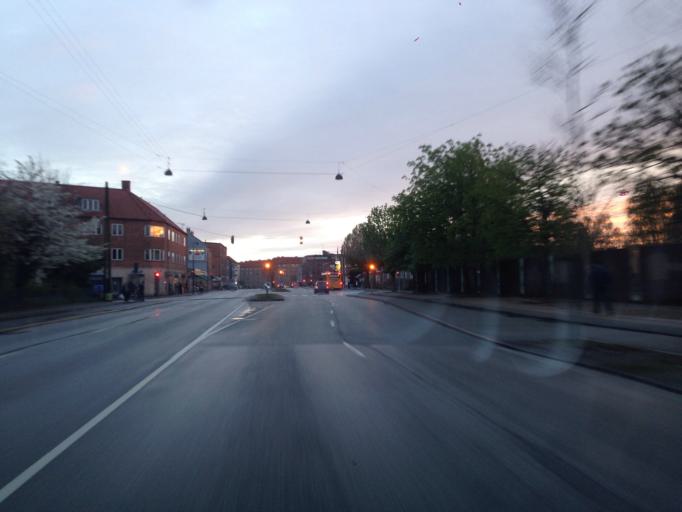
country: DK
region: Capital Region
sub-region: Frederiksberg Kommune
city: Frederiksberg
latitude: 55.7096
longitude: 12.5271
